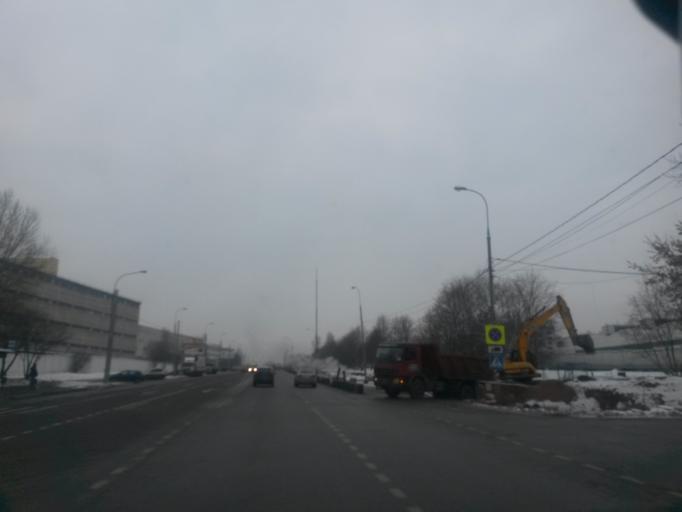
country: RU
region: Moscow
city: Mikhalkovo
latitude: 55.6833
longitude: 37.4314
